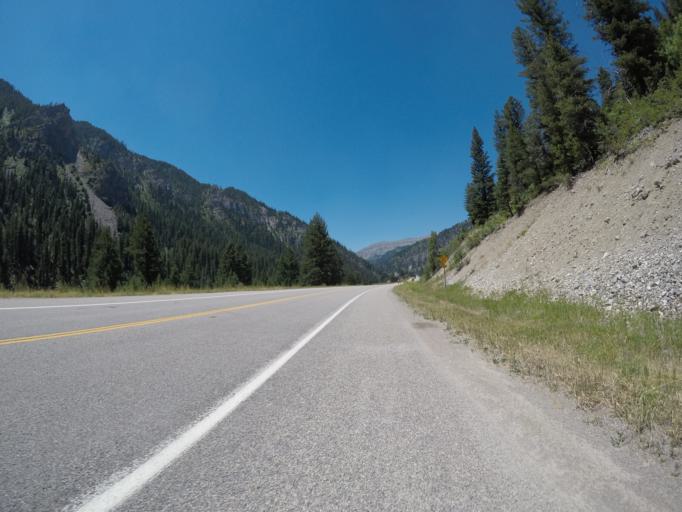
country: US
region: Wyoming
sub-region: Teton County
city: Hoback
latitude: 43.1968
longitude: -110.8870
